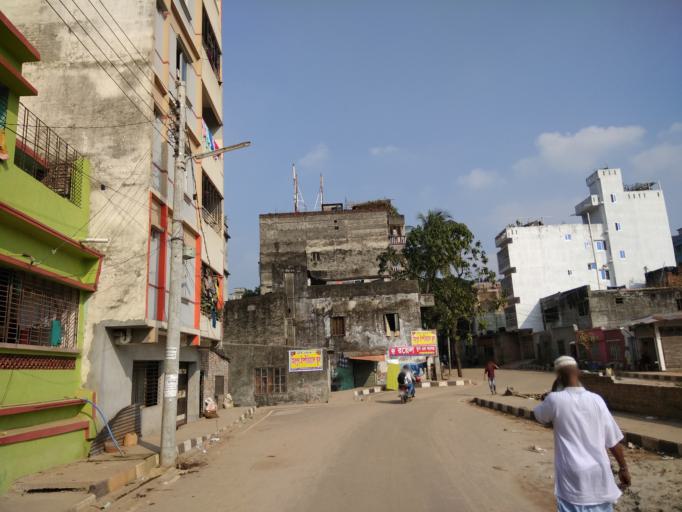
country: BD
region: Dhaka
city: Tungi
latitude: 23.8149
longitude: 90.3736
